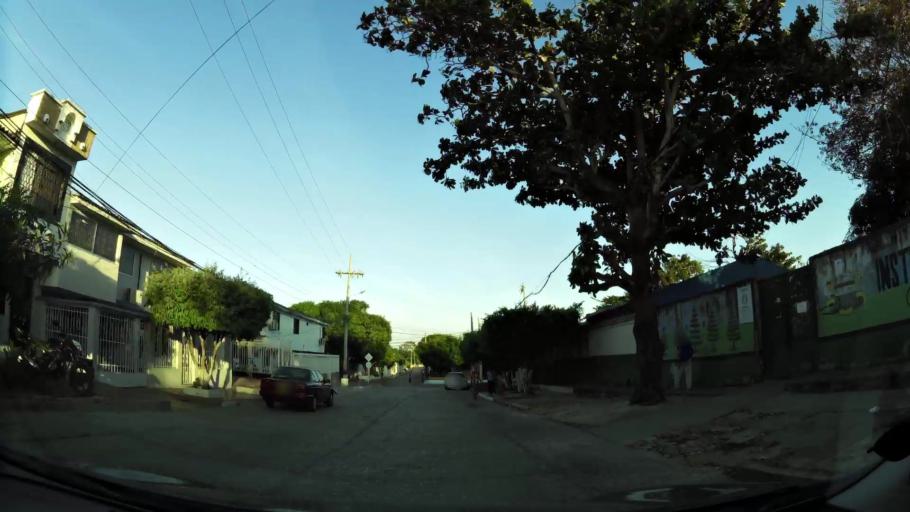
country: CO
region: Atlantico
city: Barranquilla
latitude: 10.9748
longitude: -74.7991
